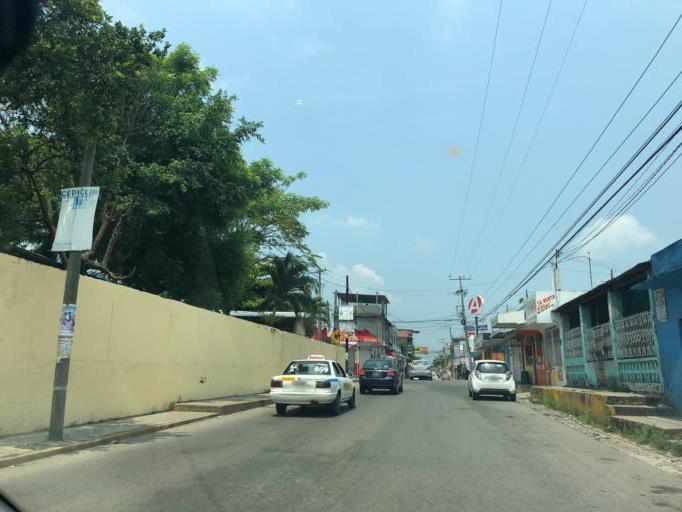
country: MX
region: Tabasco
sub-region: Cardenas
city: Cardenas
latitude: 17.9884
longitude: -93.3828
